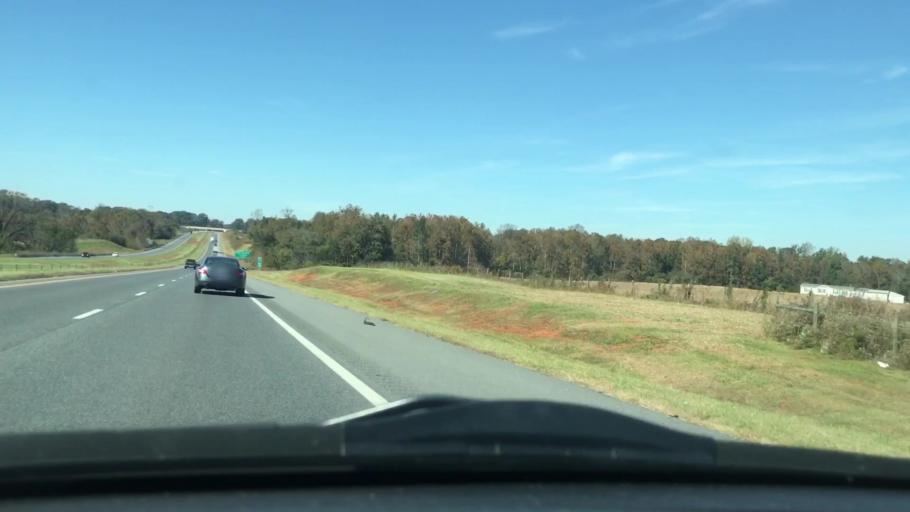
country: US
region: North Carolina
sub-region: Randolph County
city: Randleman
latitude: 35.8467
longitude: -79.8697
